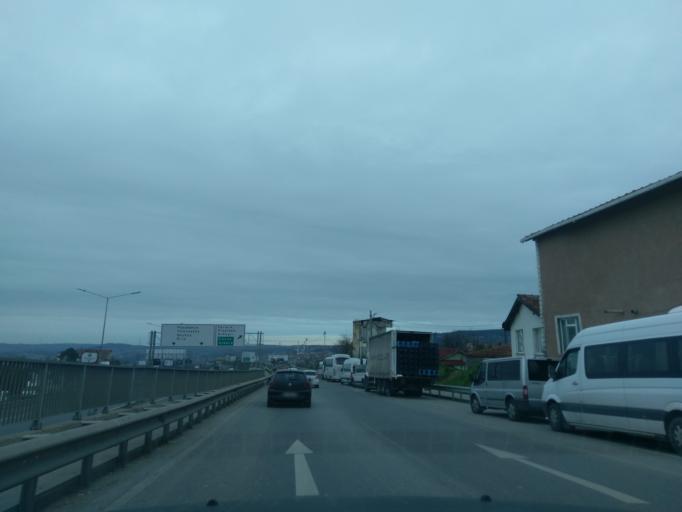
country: TR
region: Istanbul
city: Umraniye
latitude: 41.0966
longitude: 29.0971
